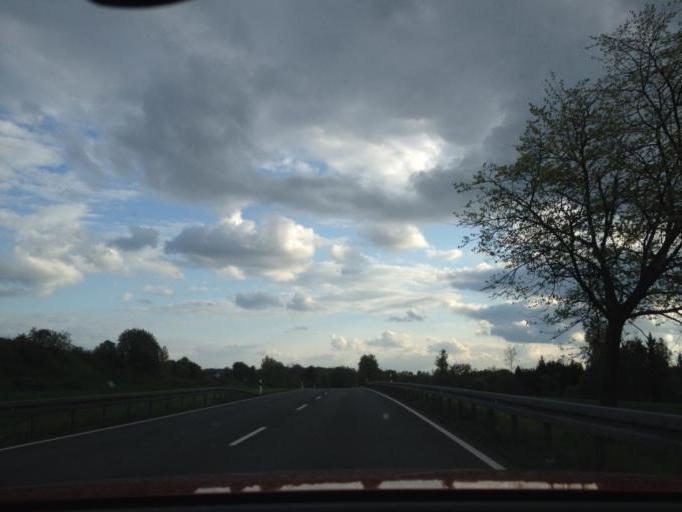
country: DE
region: Bavaria
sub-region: Upper Franconia
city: Marktredwitz
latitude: 50.0215
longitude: 12.1290
